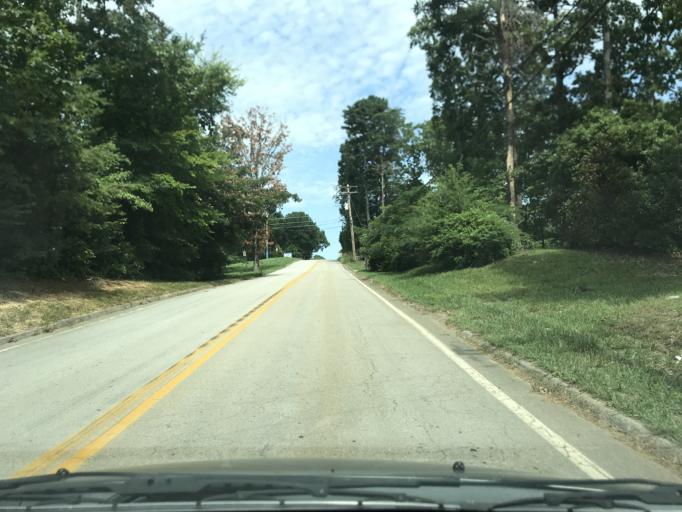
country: US
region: Tennessee
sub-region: Hamilton County
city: Lakesite
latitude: 35.1825
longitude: -85.0588
